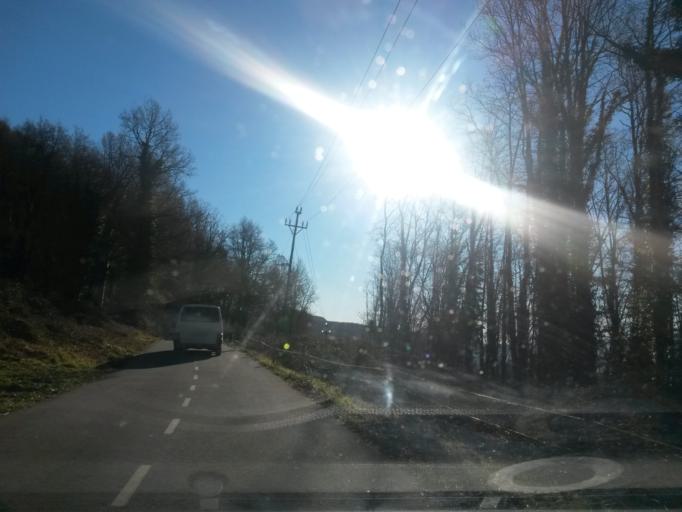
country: ES
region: Catalonia
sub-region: Provincia de Girona
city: les Planes d'Hostoles
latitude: 42.0413
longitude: 2.5104
